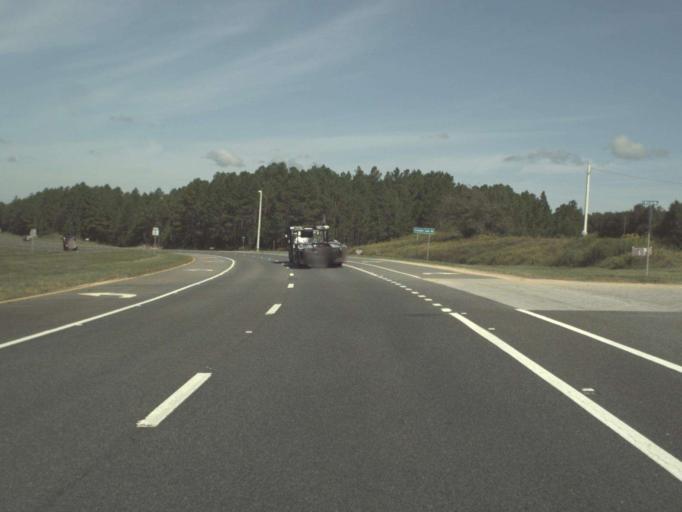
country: US
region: Florida
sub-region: Bay County
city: Youngstown
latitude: 30.5776
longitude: -85.3868
